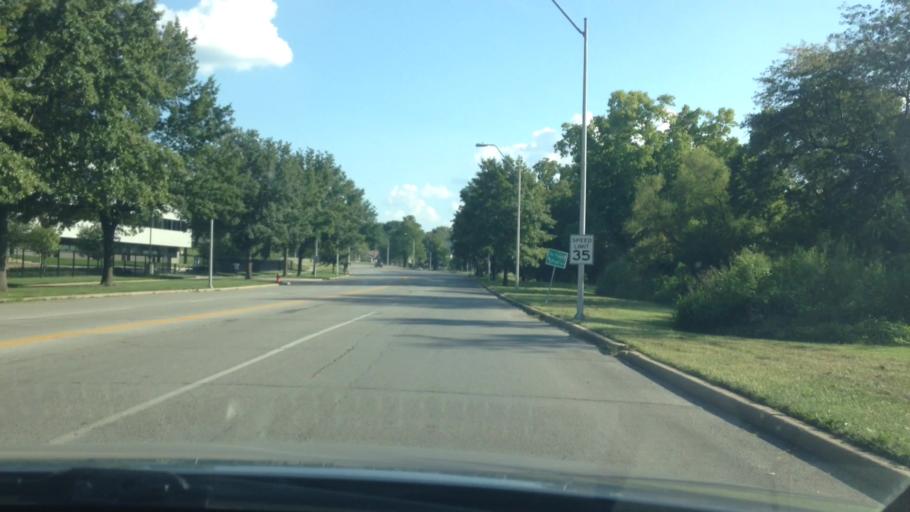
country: US
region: Kansas
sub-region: Johnson County
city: Mission Hills
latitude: 39.0121
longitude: -94.5682
